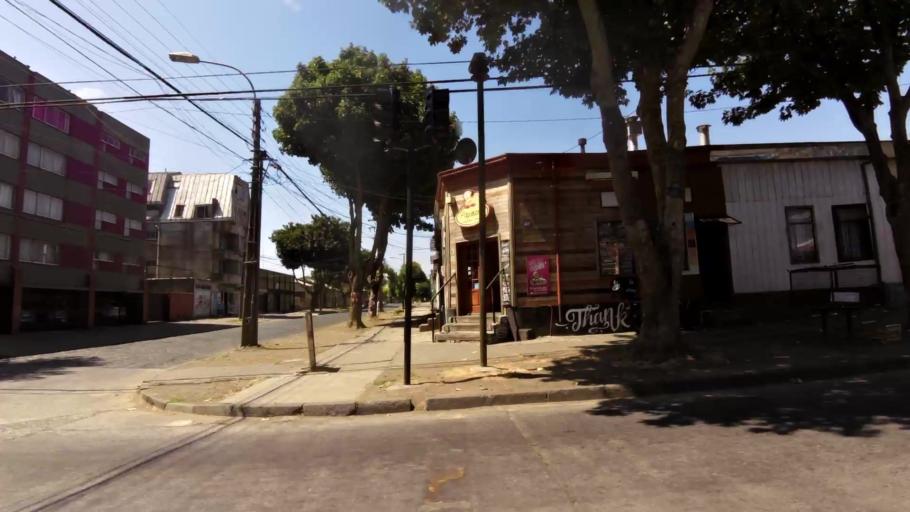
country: CL
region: Biobio
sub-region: Provincia de Concepcion
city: Concepcion
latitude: -36.8141
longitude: -73.0577
